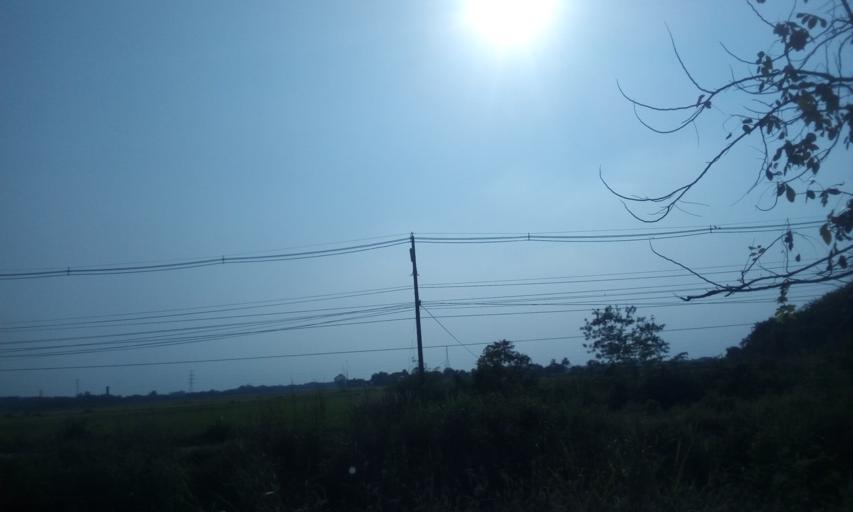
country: TH
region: Sing Buri
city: Phrom Buri
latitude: 14.8175
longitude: 100.4321
